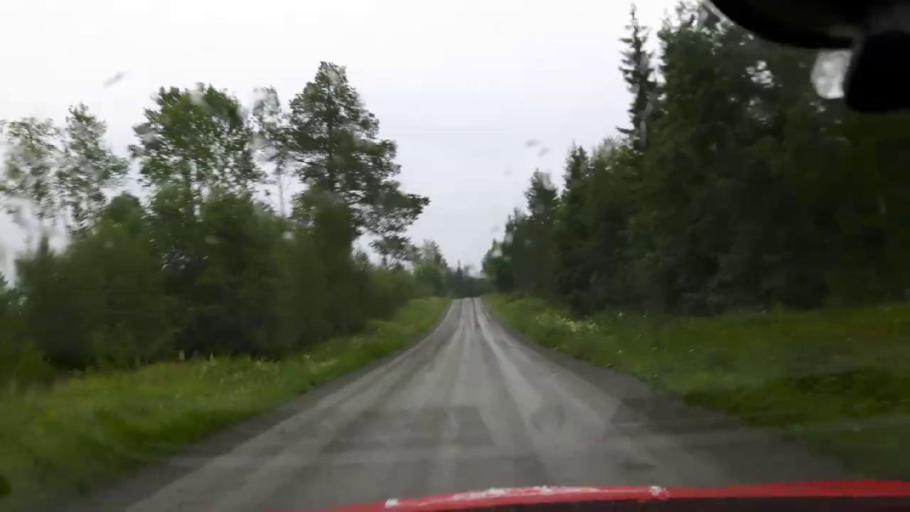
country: SE
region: Jaemtland
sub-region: OEstersunds Kommun
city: Brunflo
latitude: 62.9715
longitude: 14.8378
